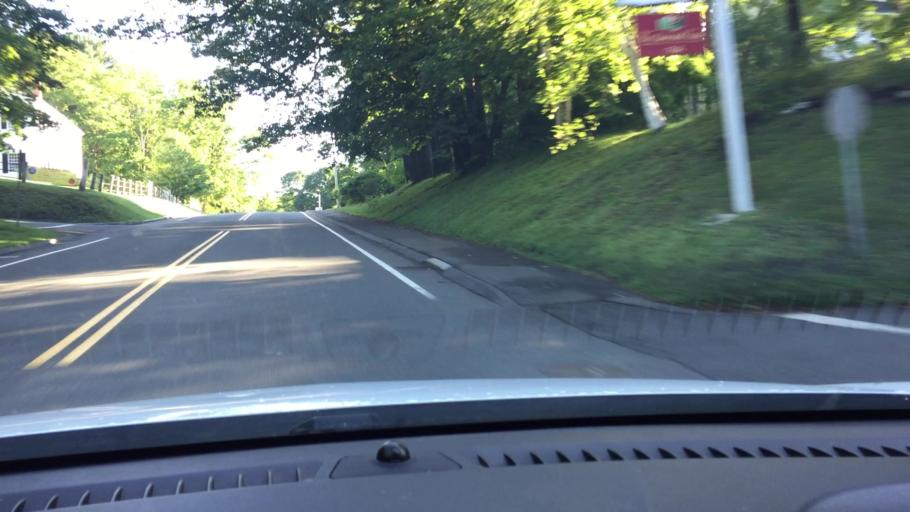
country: US
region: Massachusetts
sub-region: Berkshire County
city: Lenox
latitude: 42.3626
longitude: -73.2824
